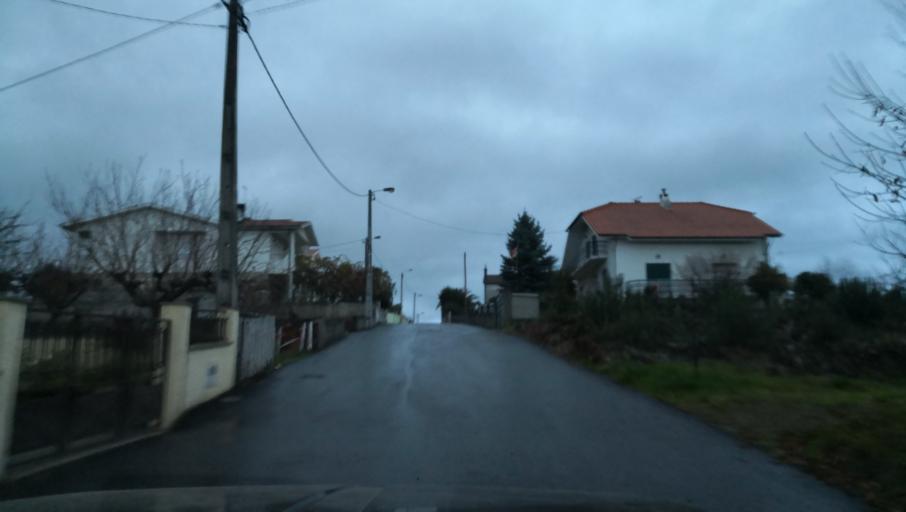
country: PT
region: Vila Real
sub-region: Vila Real
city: Vila Real
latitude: 41.2607
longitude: -7.7358
